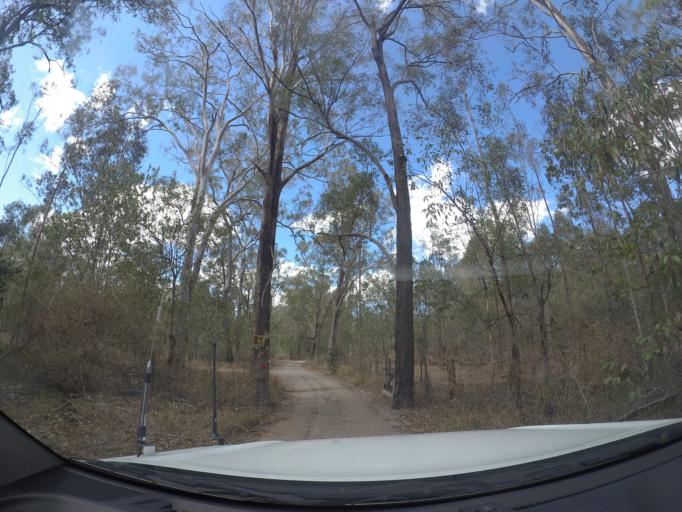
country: AU
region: Queensland
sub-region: Logan
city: North Maclean
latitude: -27.8298
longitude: 152.9677
